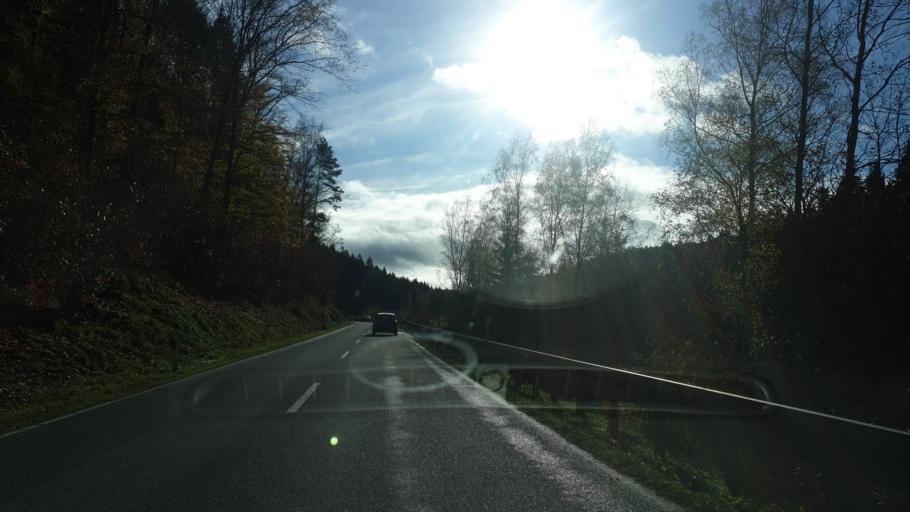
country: DE
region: Saxony
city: Bockau
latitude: 50.5681
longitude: 12.6930
